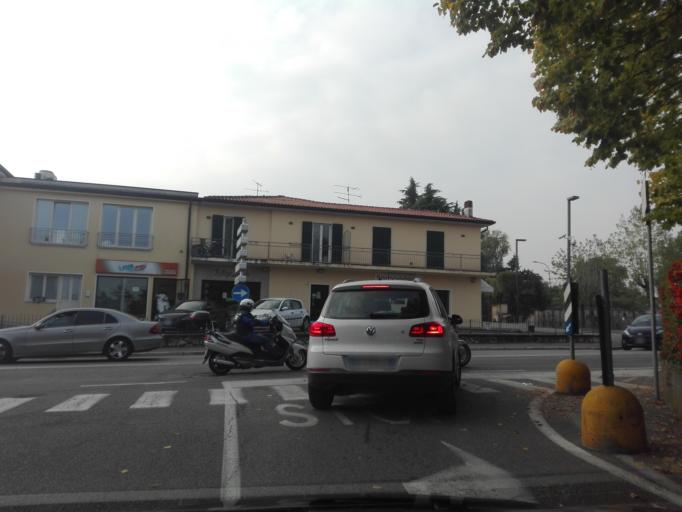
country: IT
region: Veneto
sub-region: Provincia di Verona
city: Peschiera del Garda
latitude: 45.4410
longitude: 10.6819
